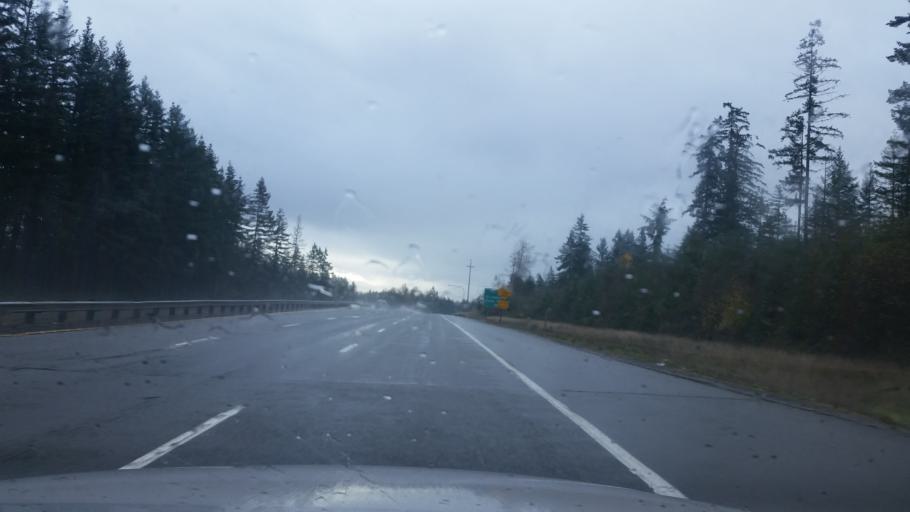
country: US
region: Washington
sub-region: King County
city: Maple Valley
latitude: 47.4012
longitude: -122.0449
